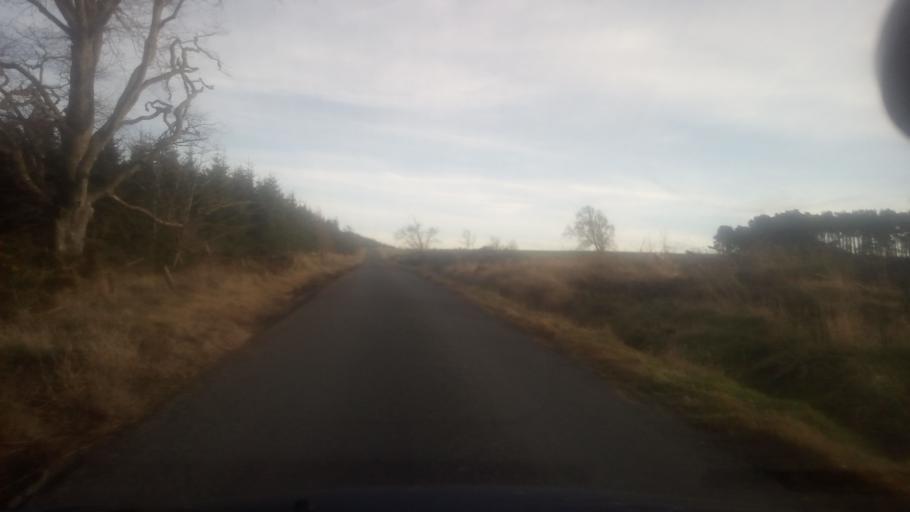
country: GB
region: Scotland
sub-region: The Scottish Borders
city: Jedburgh
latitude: 55.4029
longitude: -2.6002
